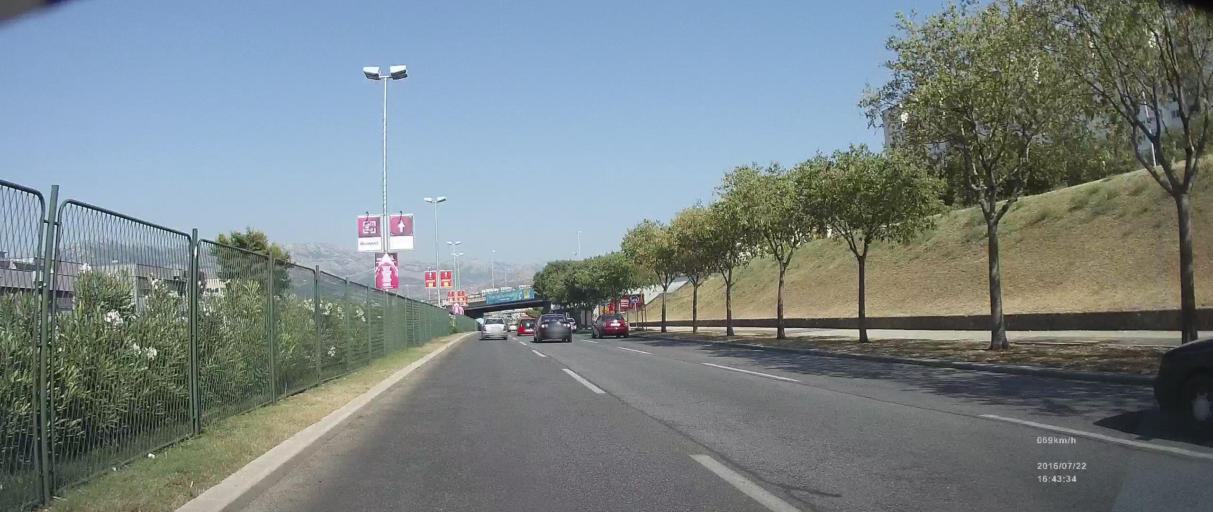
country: HR
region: Splitsko-Dalmatinska
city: Vranjic
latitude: 43.5193
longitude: 16.4715
